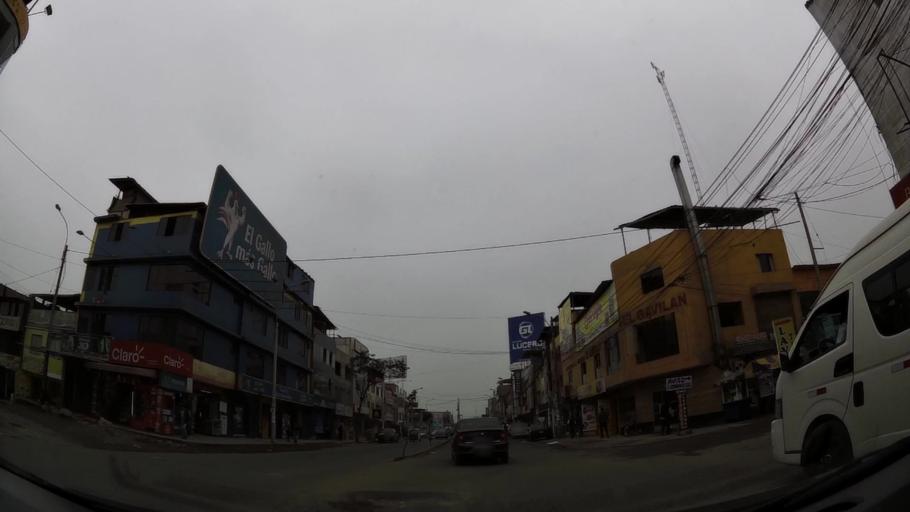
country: PE
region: Lima
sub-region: Lima
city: Surco
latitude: -12.2096
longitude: -76.9389
